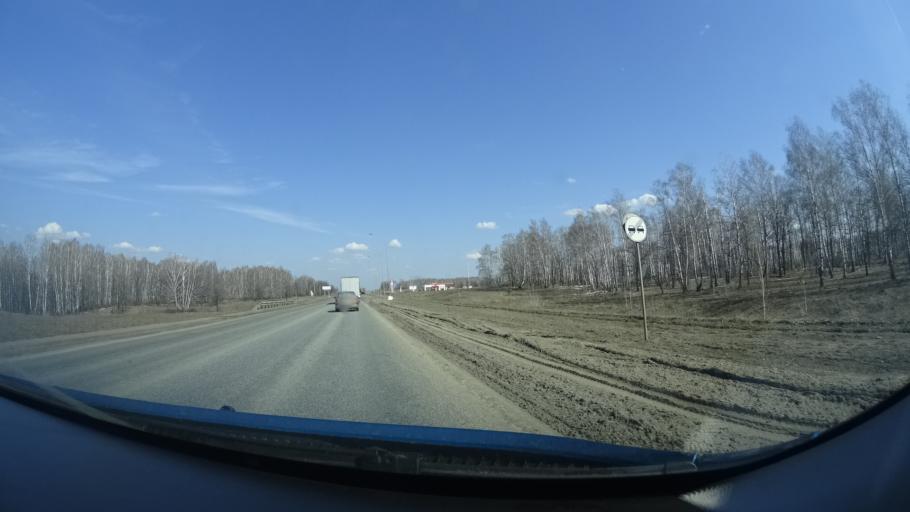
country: RU
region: Bashkortostan
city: Kandry
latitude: 54.5869
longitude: 54.2633
